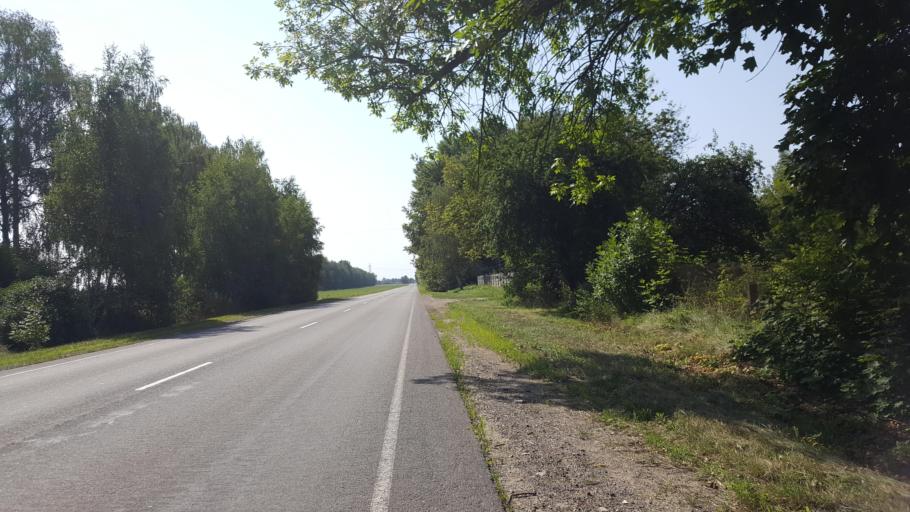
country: BY
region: Brest
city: Zhabinka
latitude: 52.2211
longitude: 23.9922
